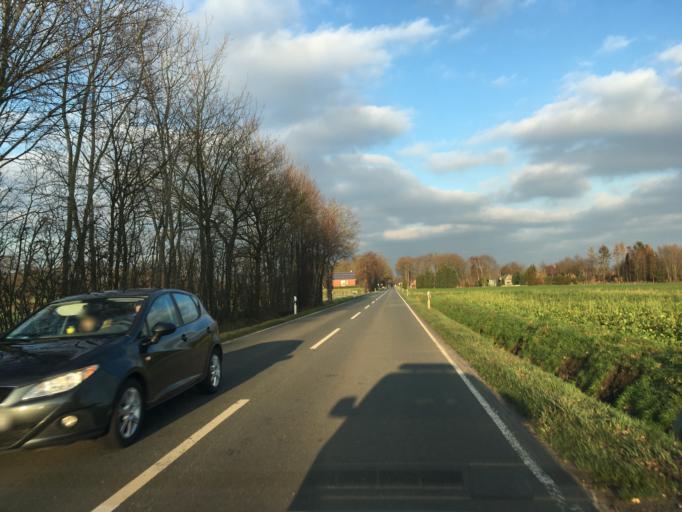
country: DE
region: North Rhine-Westphalia
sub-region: Regierungsbezirk Munster
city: Gronau
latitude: 52.1539
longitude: 7.0204
